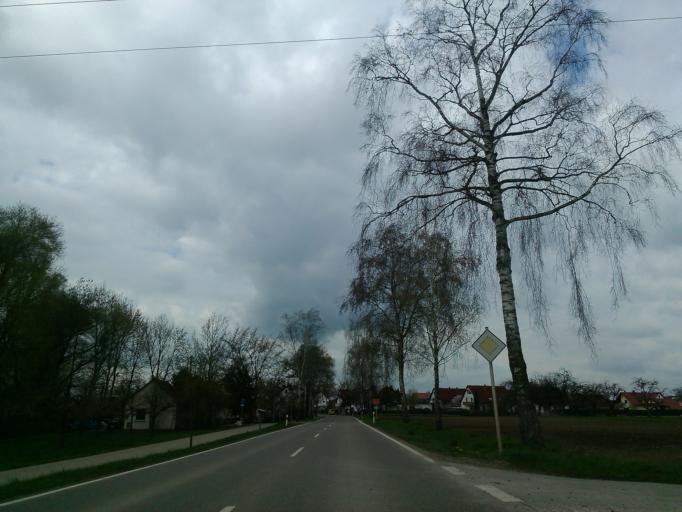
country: DE
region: Bavaria
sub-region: Swabia
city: Leipheim
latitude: 48.4627
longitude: 10.1962
